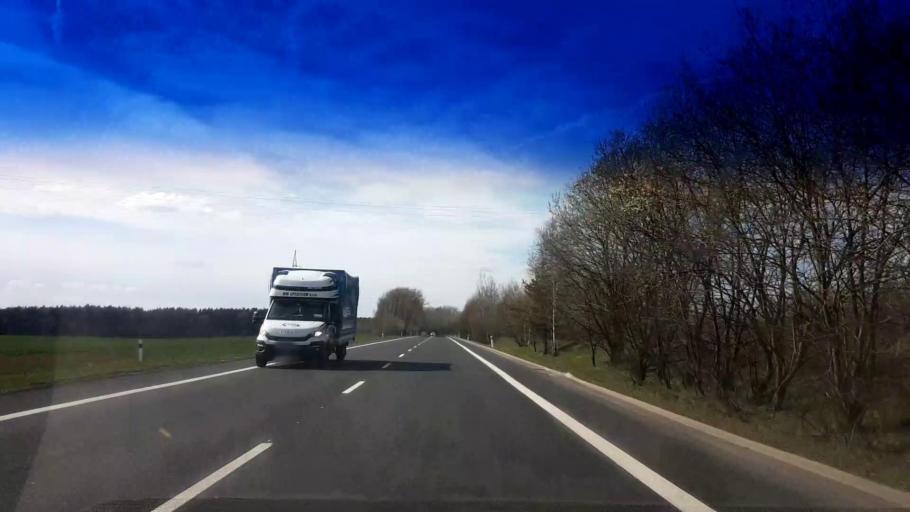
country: CZ
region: Karlovarsky
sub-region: Okres Cheb
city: Frantiskovy Lazne
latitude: 50.0958
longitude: 12.3369
